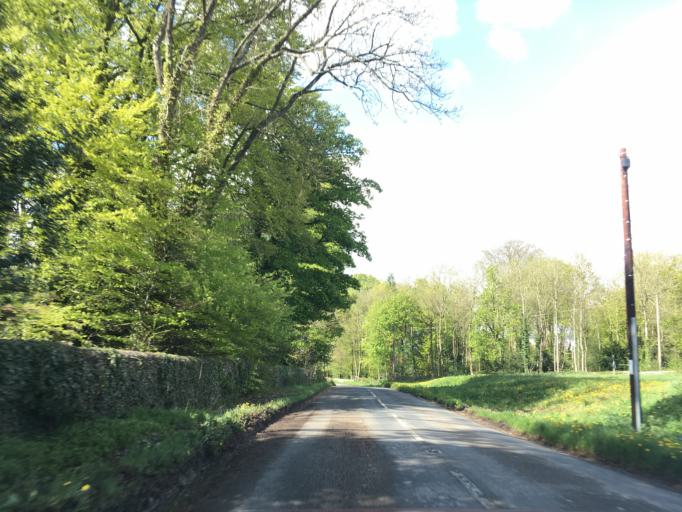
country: GB
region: England
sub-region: Gloucestershire
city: Minchinhampton
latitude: 51.6949
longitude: -2.1679
